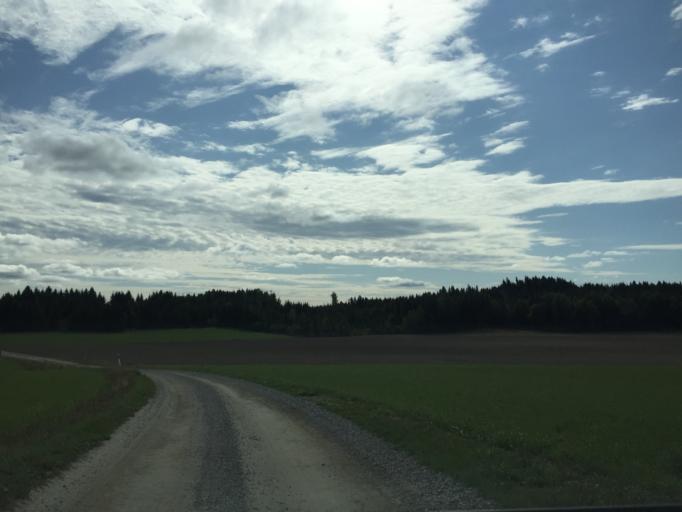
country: NO
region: Ostfold
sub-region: Hobol
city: Elvestad
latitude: 59.6323
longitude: 10.8889
